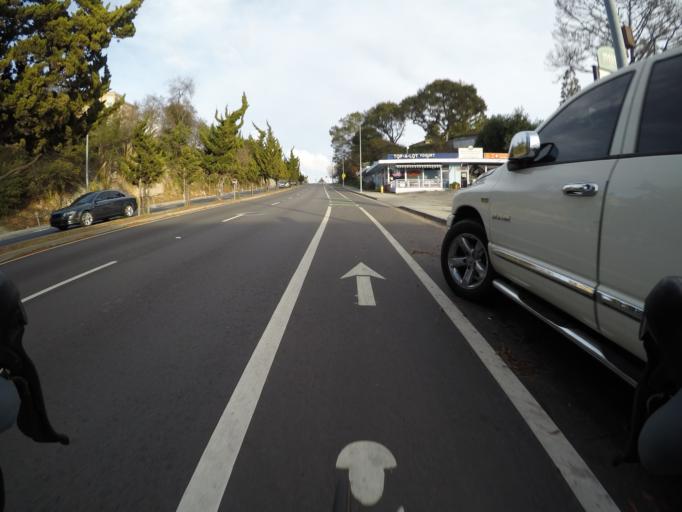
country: US
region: California
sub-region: Santa Cruz County
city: Santa Cruz
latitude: 36.9810
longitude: -122.0163
